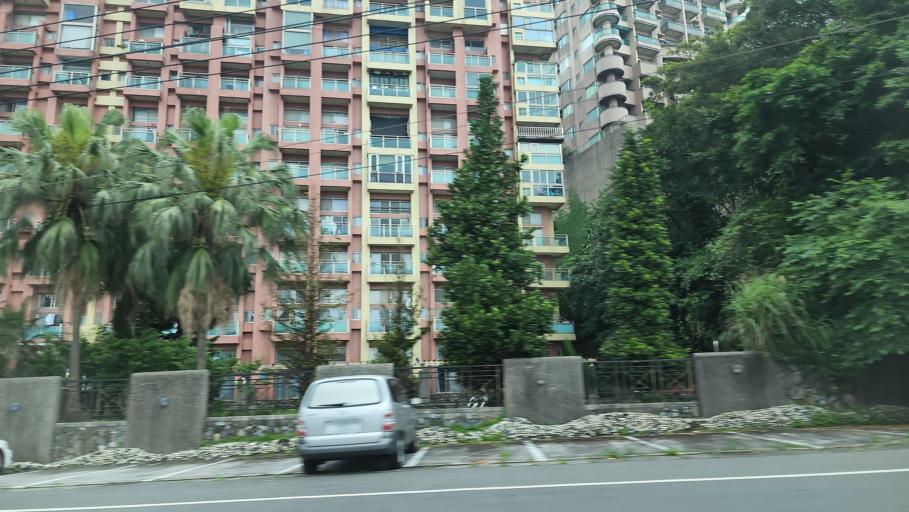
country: TW
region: Taiwan
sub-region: Keelung
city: Keelung
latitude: 25.1932
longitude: 121.6806
